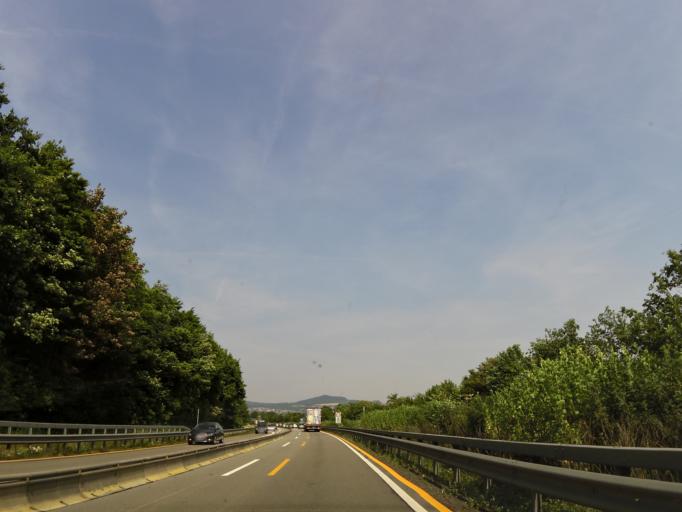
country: DE
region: Rheinland-Pfalz
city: Kretz
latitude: 50.3881
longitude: 7.3741
